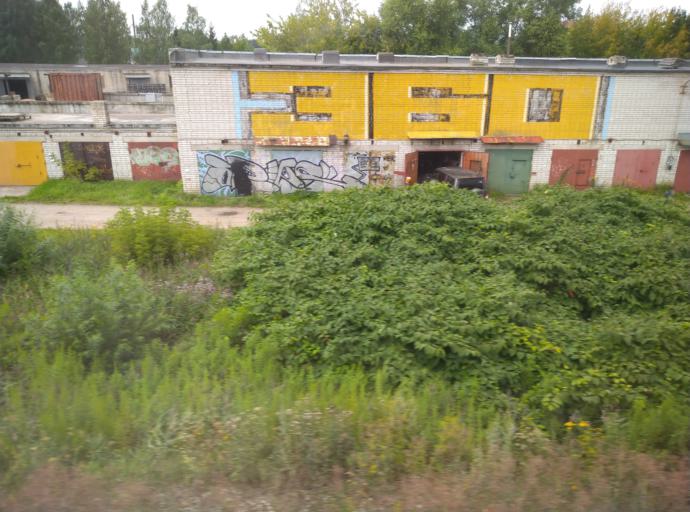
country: RU
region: Jaroslavl
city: Yaroslavl
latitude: 57.5935
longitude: 39.8914
